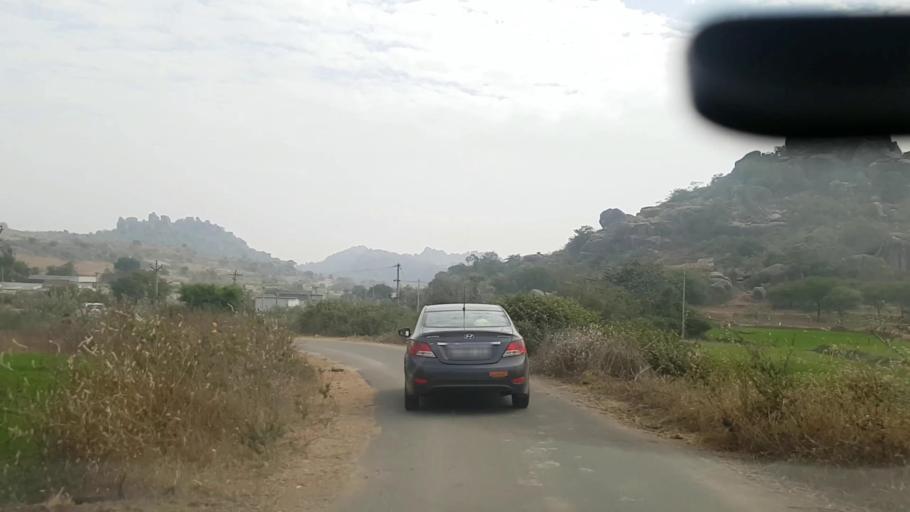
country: IN
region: Telangana
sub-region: Rangareddi
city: Lal Bahadur Nagar
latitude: 17.1789
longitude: 78.7798
